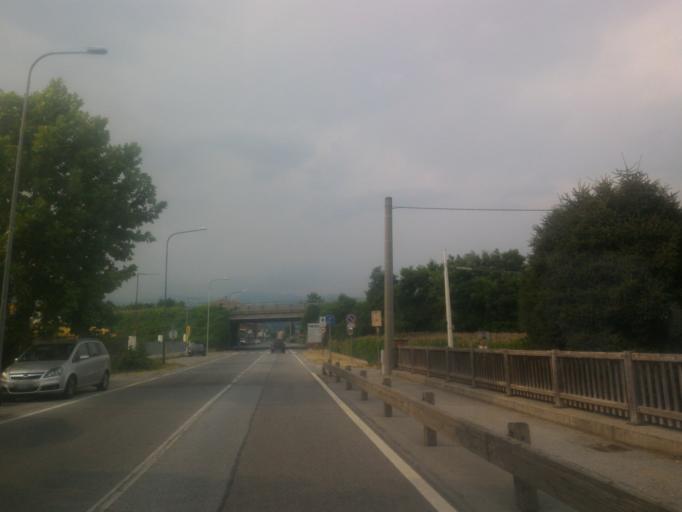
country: IT
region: Piedmont
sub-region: Provincia di Torino
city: Pinerolo
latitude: 44.8705
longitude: 7.3346
